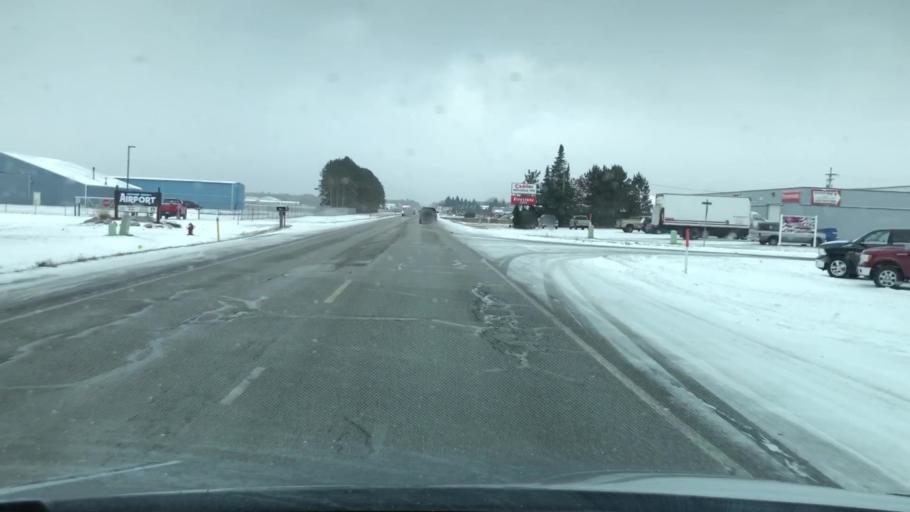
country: US
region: Michigan
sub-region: Wexford County
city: Cadillac
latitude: 44.2814
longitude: -85.4163
